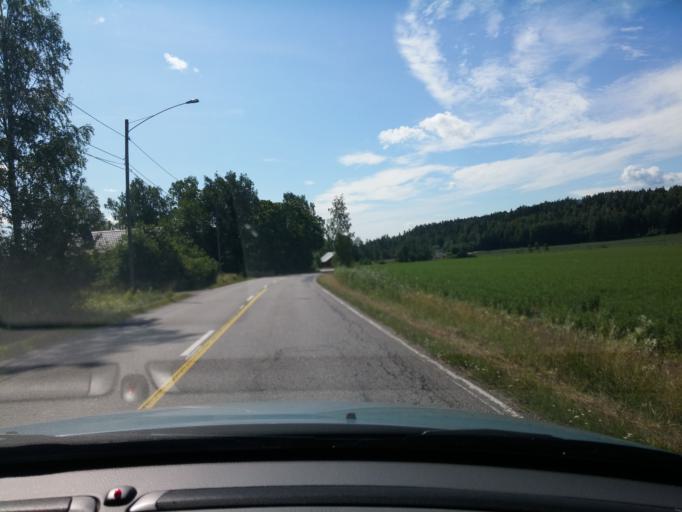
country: FI
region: Uusimaa
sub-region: Porvoo
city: Askola
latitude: 60.4440
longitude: 25.5885
